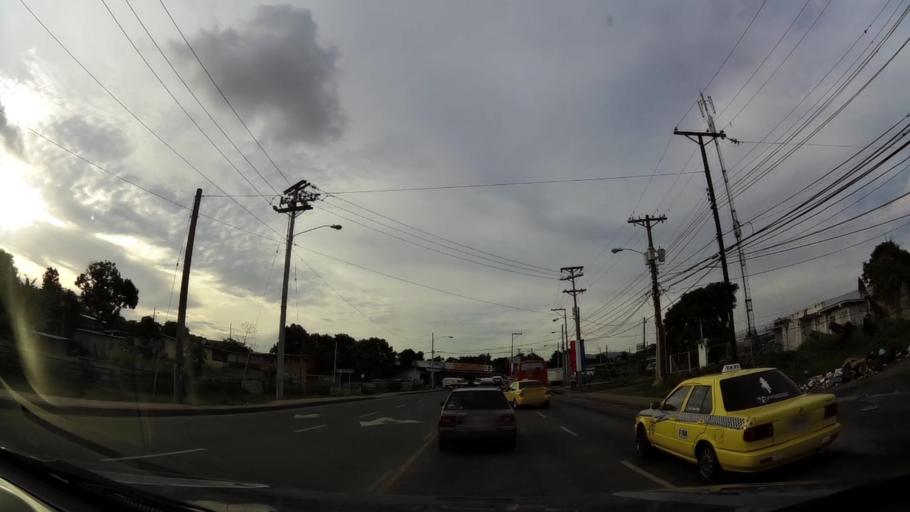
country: PA
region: Panama
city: Tocumen
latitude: 9.0968
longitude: -79.3699
